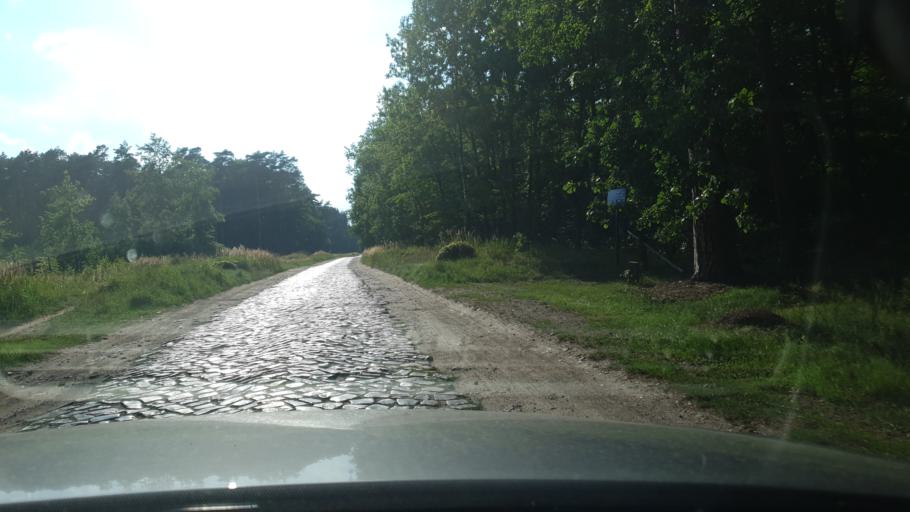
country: PL
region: Kujawsko-Pomorskie
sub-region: Grudziadz
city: Grudziadz
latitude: 53.4415
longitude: 18.7631
